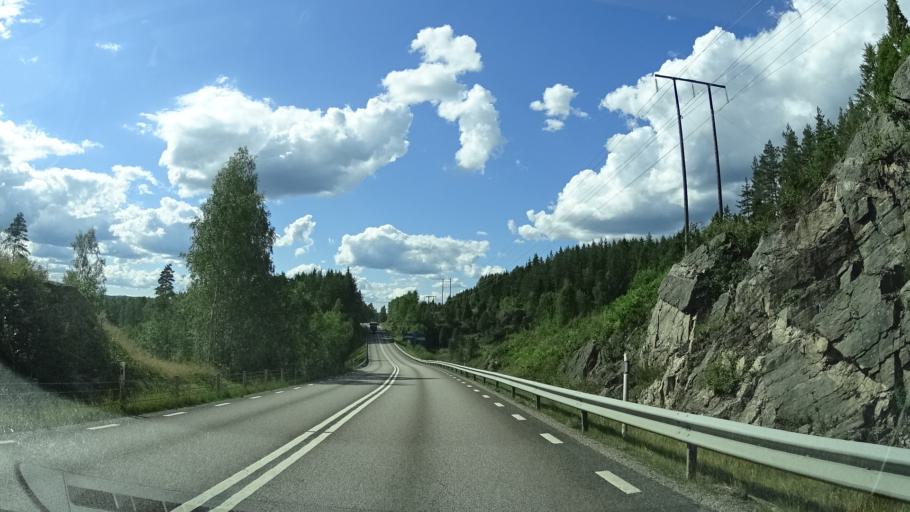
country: SE
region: Vaermland
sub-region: Arjangs Kommun
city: Toecksfors
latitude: 59.5029
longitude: 11.8725
